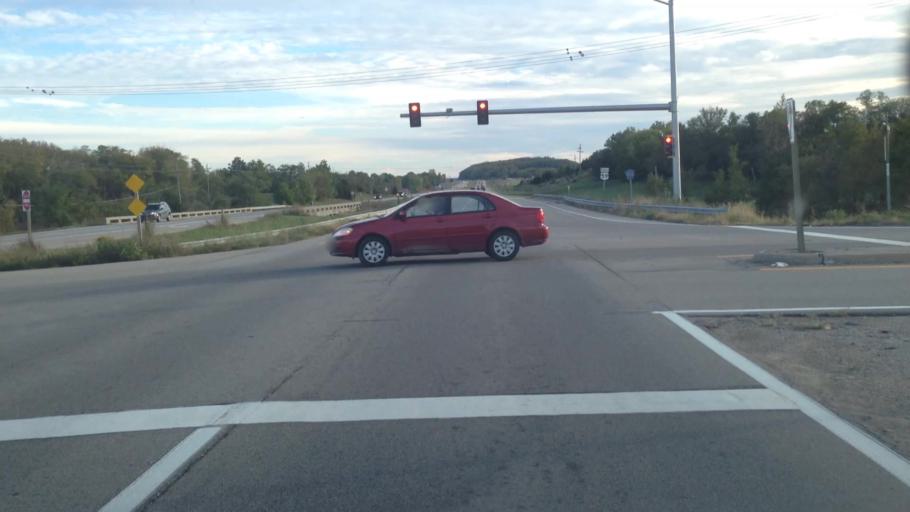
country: US
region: Kansas
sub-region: Douglas County
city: Lawrence
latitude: 38.9088
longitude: -95.2608
